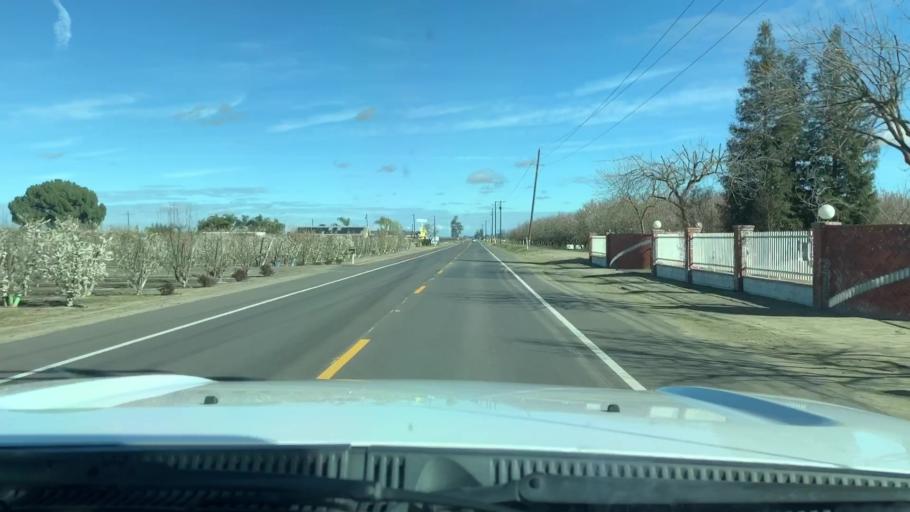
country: US
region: California
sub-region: Fresno County
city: Laton
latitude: 36.5011
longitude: -119.6830
